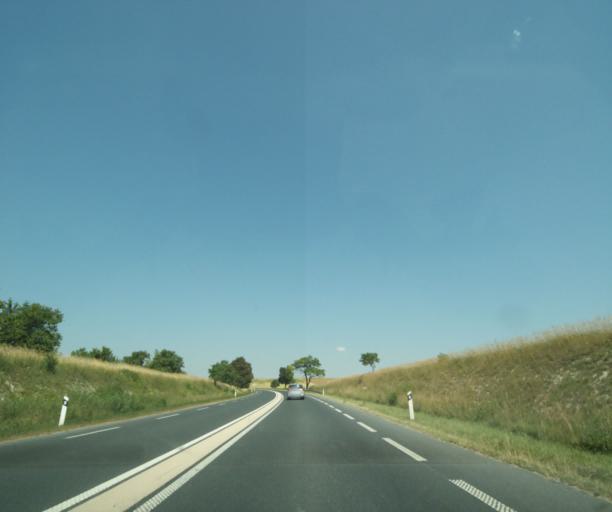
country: FR
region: Champagne-Ardenne
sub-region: Departement de la Marne
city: Mourmelon-le-Grand
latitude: 49.0689
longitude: 4.2951
